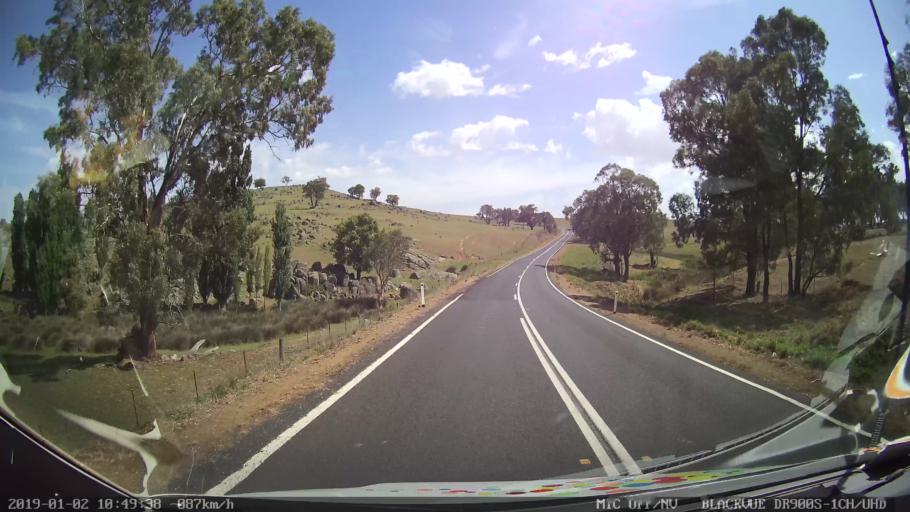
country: AU
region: New South Wales
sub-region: Cootamundra
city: Cootamundra
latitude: -34.7217
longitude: 148.2760
